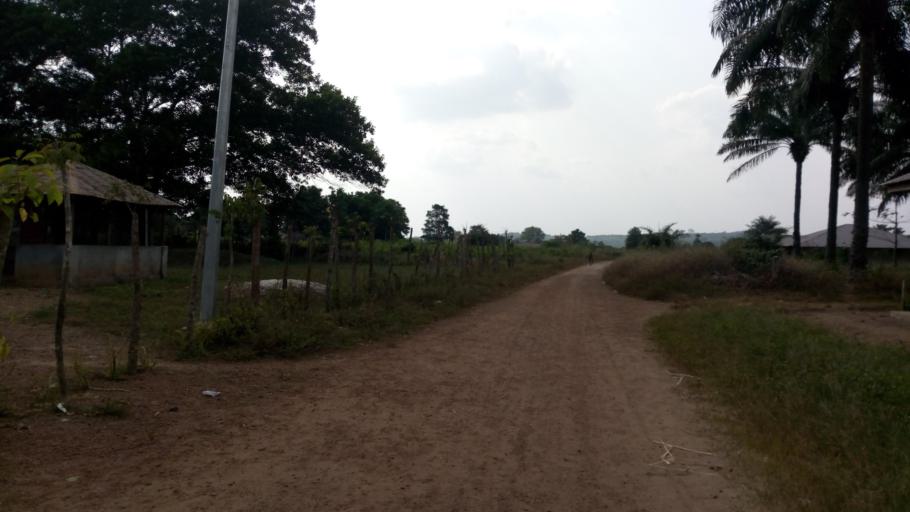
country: SL
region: Southern Province
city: Mogbwemo
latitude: 7.7650
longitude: -12.3135
